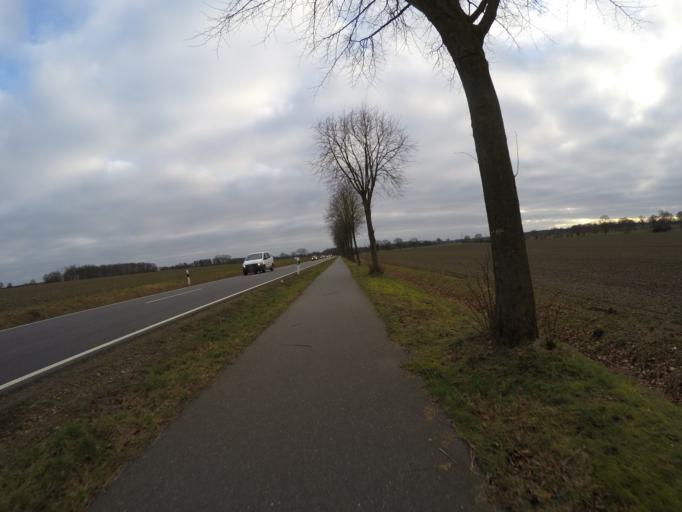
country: DE
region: Schleswig-Holstein
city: Alveslohe
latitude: 53.7730
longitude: 9.9060
